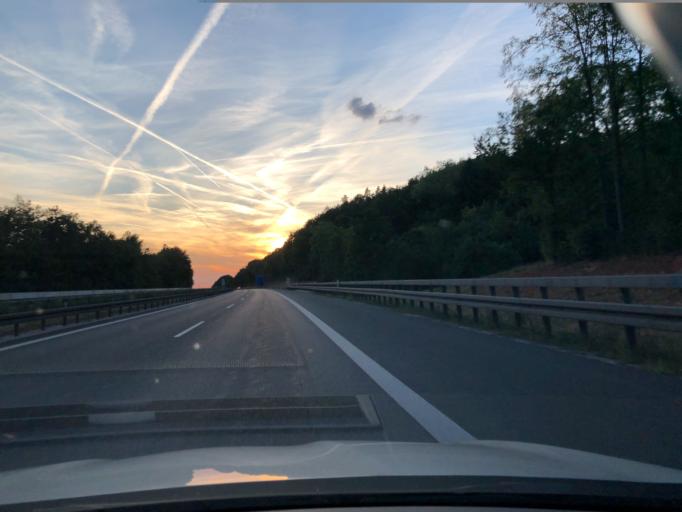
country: DE
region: Bavaria
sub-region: Regierungsbezirk Mittelfranken
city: Altdorf
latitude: 49.4055
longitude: 11.3626
